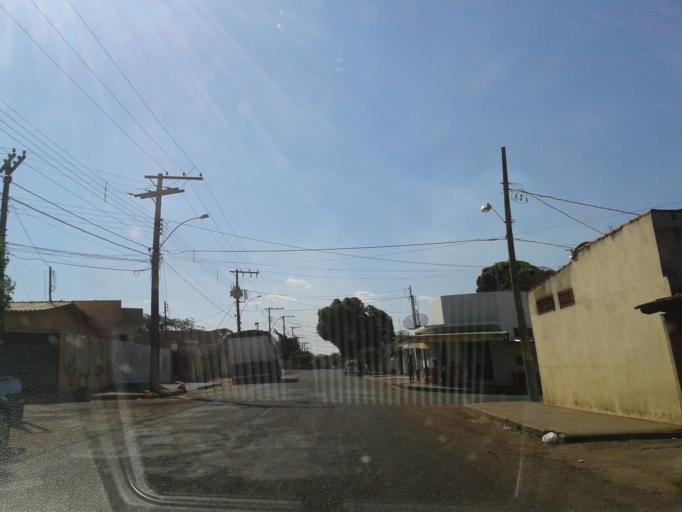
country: BR
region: Minas Gerais
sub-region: Araguari
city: Araguari
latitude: -18.6567
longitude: -48.1802
